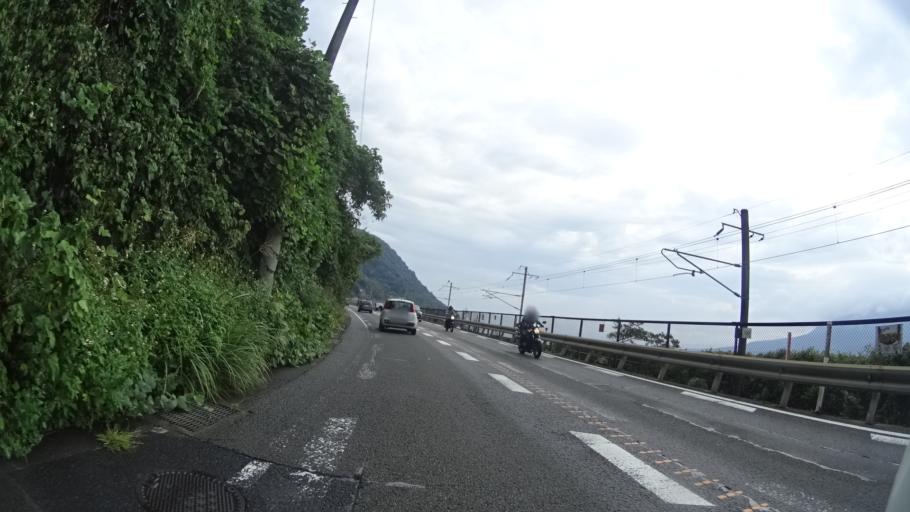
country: JP
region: Kagoshima
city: Kagoshima-shi
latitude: 31.6197
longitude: 130.5839
